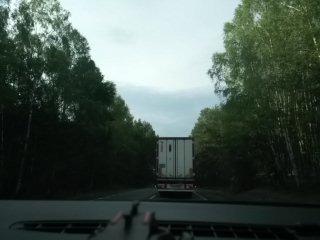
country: PL
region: Subcarpathian Voivodeship
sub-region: Powiat nizanski
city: Jarocin
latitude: 50.6319
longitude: 22.2865
